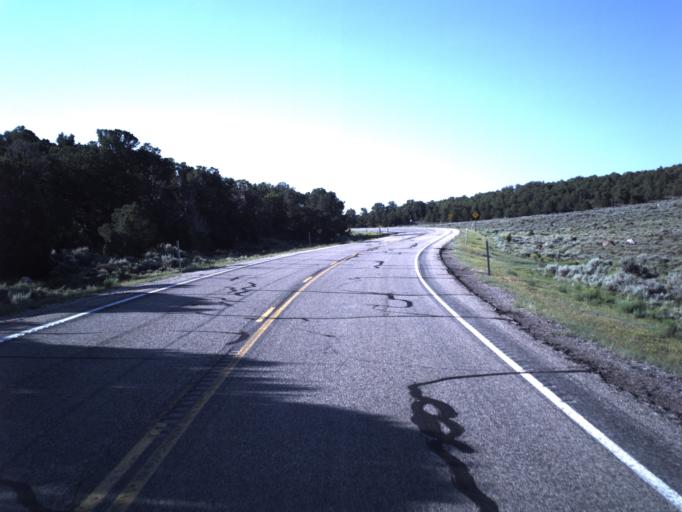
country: US
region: Utah
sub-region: Wayne County
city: Loa
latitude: 38.6969
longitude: -111.3968
